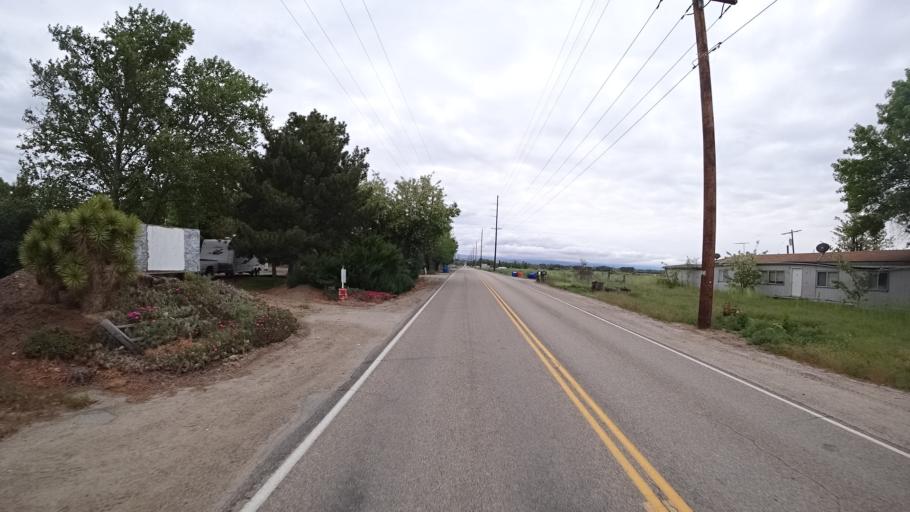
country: US
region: Idaho
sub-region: Ada County
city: Star
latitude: 43.7211
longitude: -116.4339
